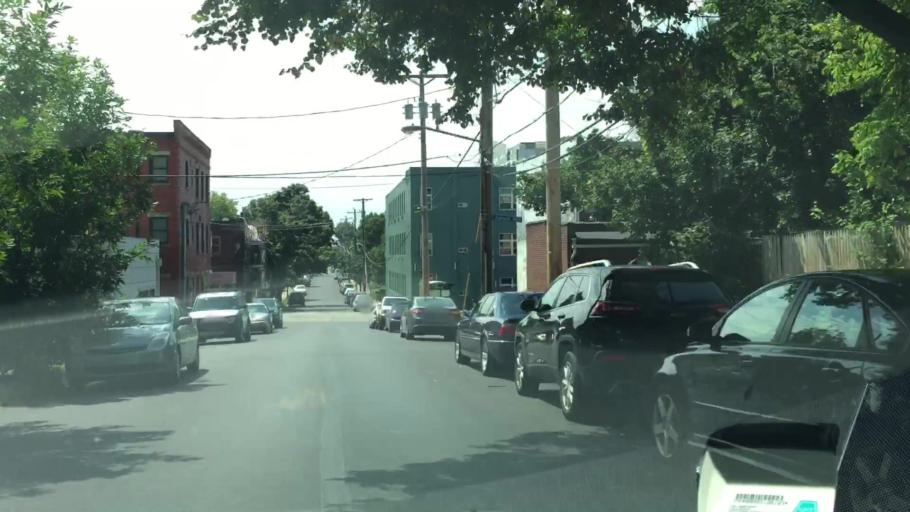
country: US
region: Pennsylvania
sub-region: Allegheny County
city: Sharpsburg
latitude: 40.4767
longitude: -79.9204
